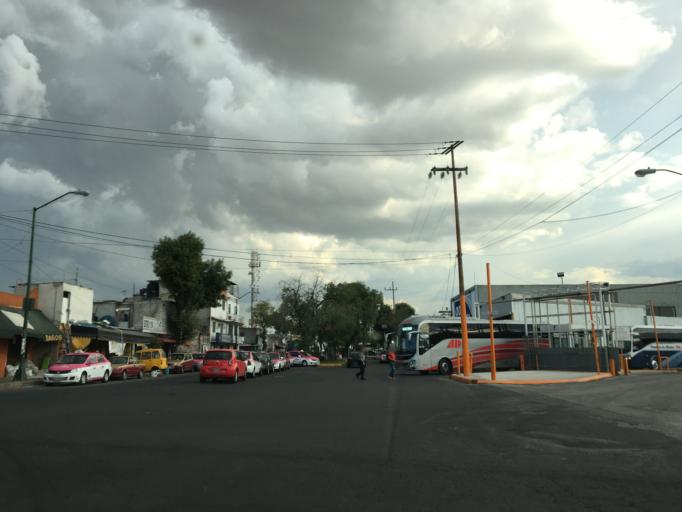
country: MX
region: Mexico
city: Colonia Lindavista
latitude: 19.4797
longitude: -99.1377
